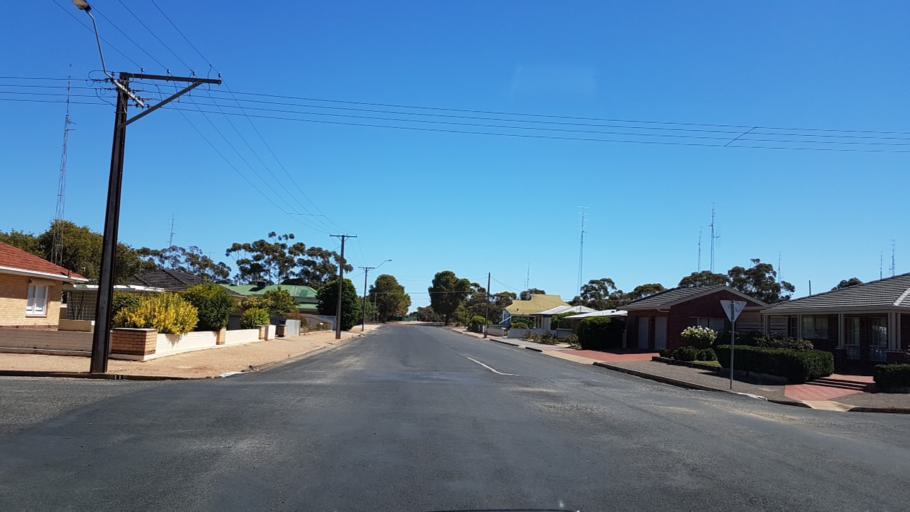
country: AU
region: South Australia
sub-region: Copper Coast
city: Kadina
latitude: -33.9597
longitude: 137.7137
